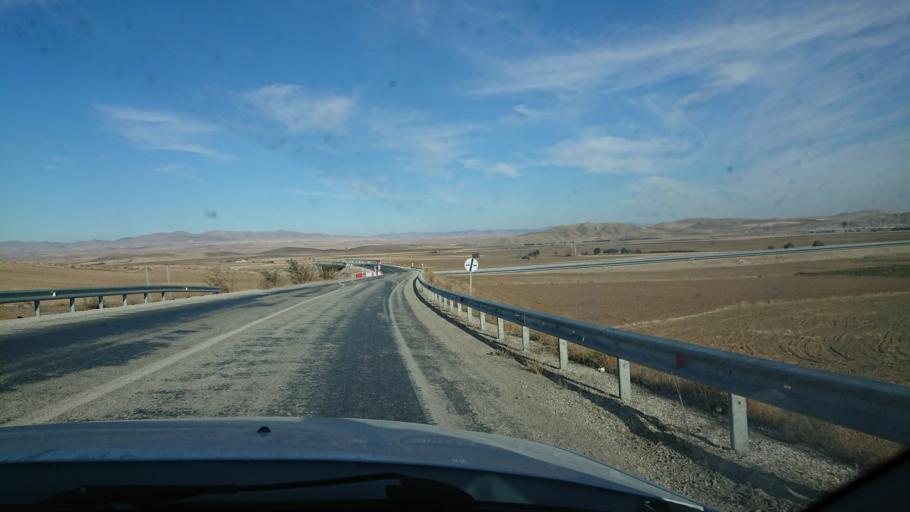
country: TR
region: Aksaray
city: Sariyahsi
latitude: 38.9971
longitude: 33.8512
